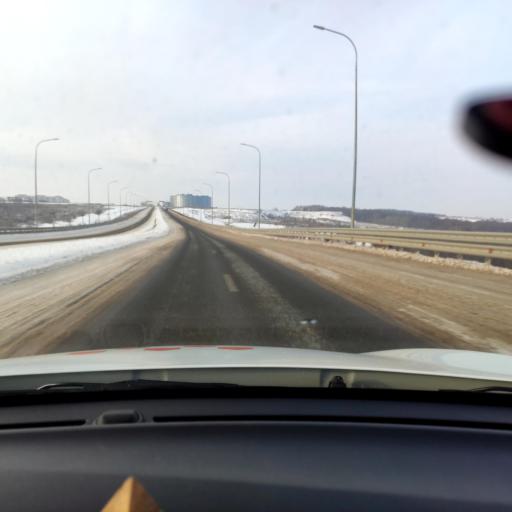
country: RU
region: Tatarstan
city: Sviyazhsk
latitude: 55.7452
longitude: 48.7703
